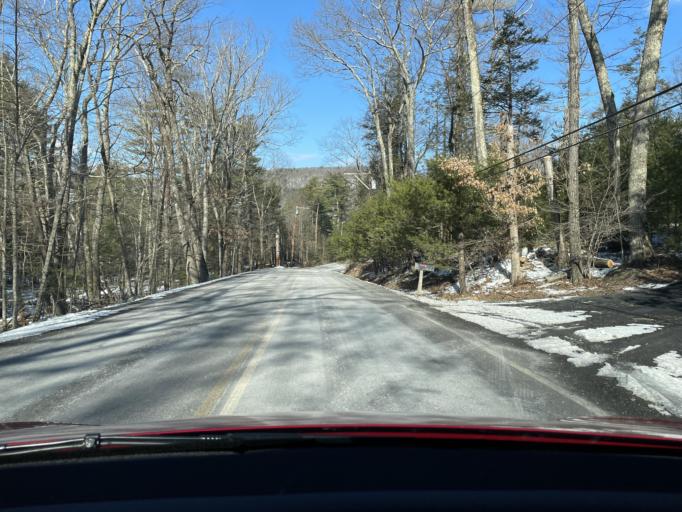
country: US
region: New York
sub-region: Ulster County
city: Woodstock
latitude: 42.0523
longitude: -74.1529
